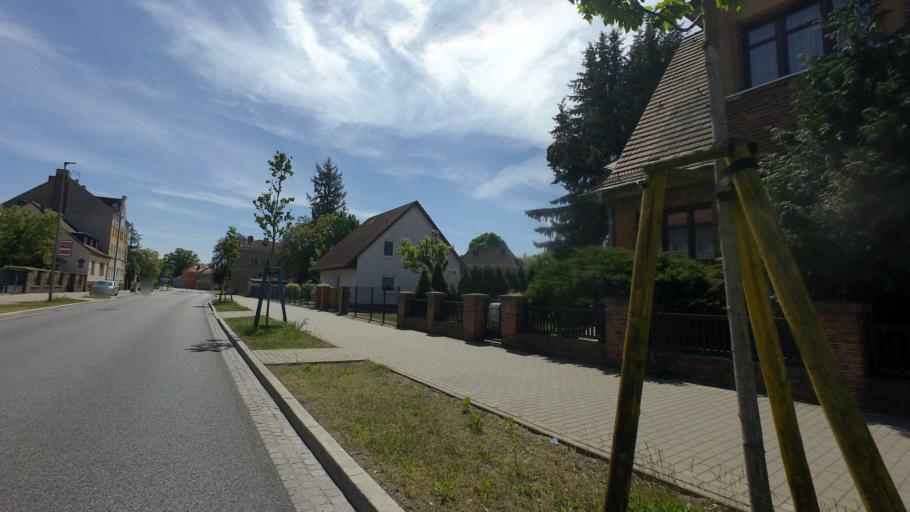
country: DE
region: Brandenburg
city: Luckenwalde
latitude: 52.0973
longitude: 13.1622
